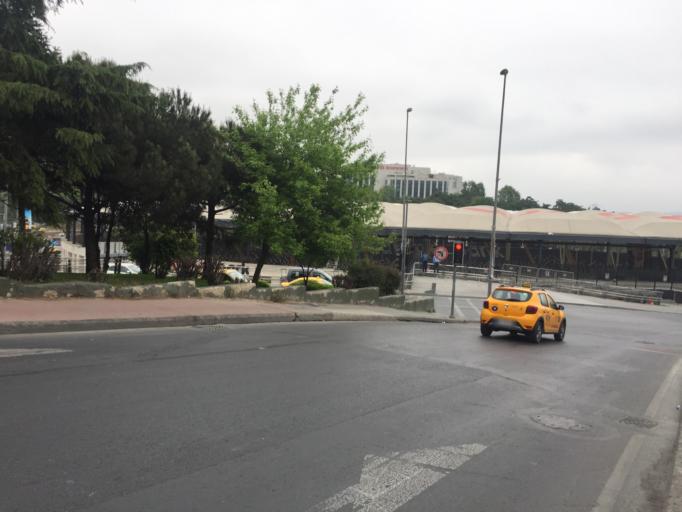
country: TR
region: Istanbul
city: Sisli
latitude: 41.0392
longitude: 28.9925
